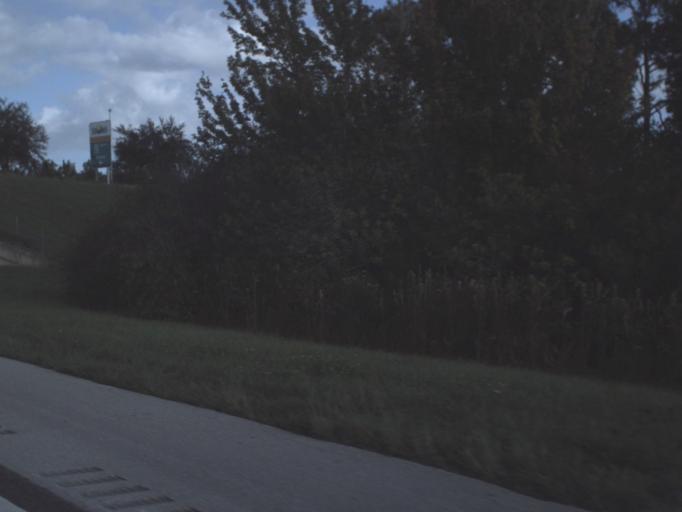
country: US
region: Florida
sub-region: Osceola County
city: Saint Cloud
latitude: 28.2205
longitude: -81.3162
